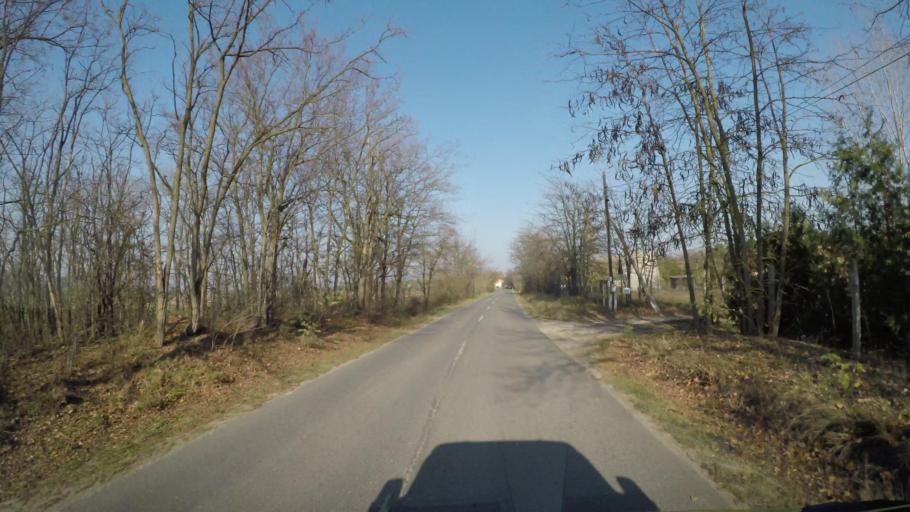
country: HU
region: Pest
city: Leanyfalu
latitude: 47.7010
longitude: 19.1054
